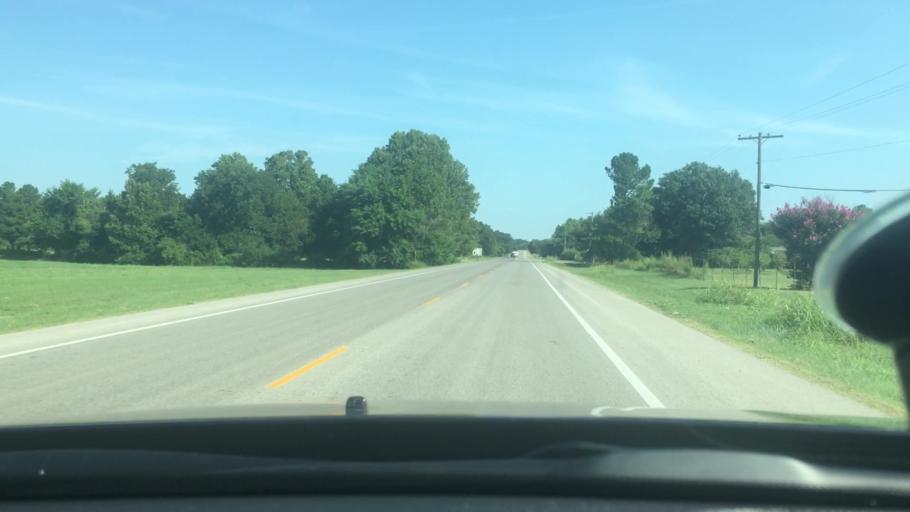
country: US
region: Oklahoma
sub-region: Garvin County
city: Wynnewood
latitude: 34.6687
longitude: -97.2056
